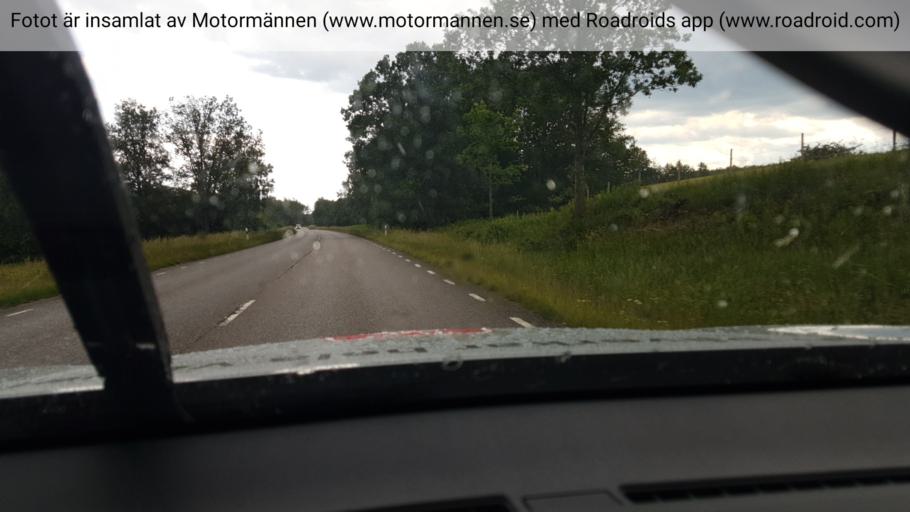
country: SE
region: Vaestra Goetaland
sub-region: Hjo Kommun
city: Hjo
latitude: 58.2994
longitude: 14.2568
